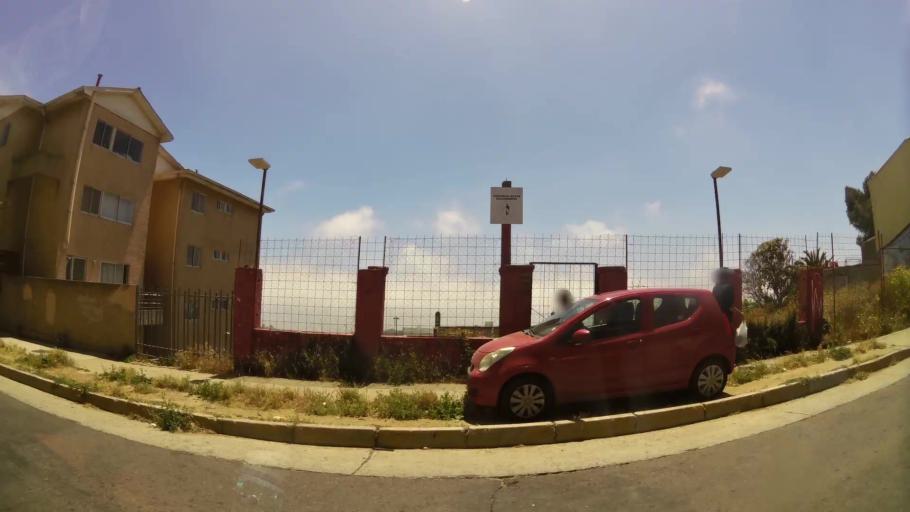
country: CL
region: Valparaiso
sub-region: Provincia de Valparaiso
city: Valparaiso
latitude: -33.0300
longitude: -71.6448
